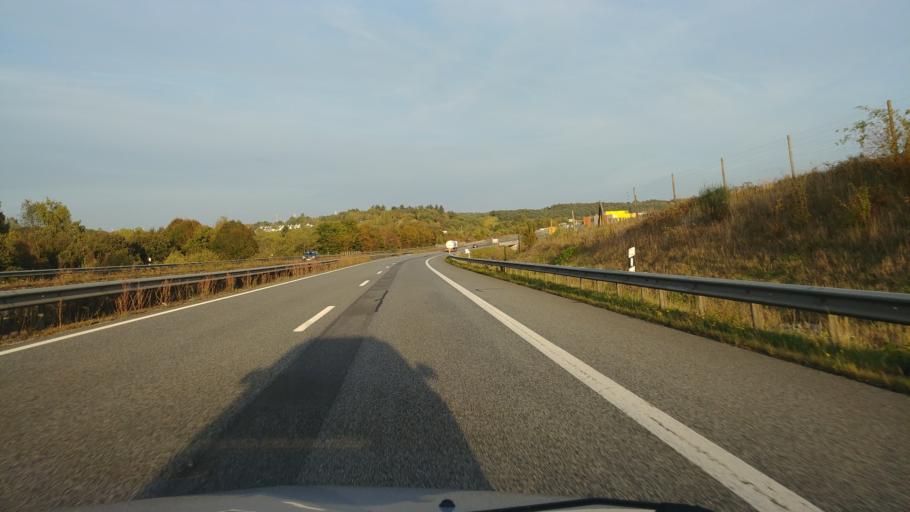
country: DE
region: Rheinland-Pfalz
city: Ohlweiler
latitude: 49.9743
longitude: 7.5051
